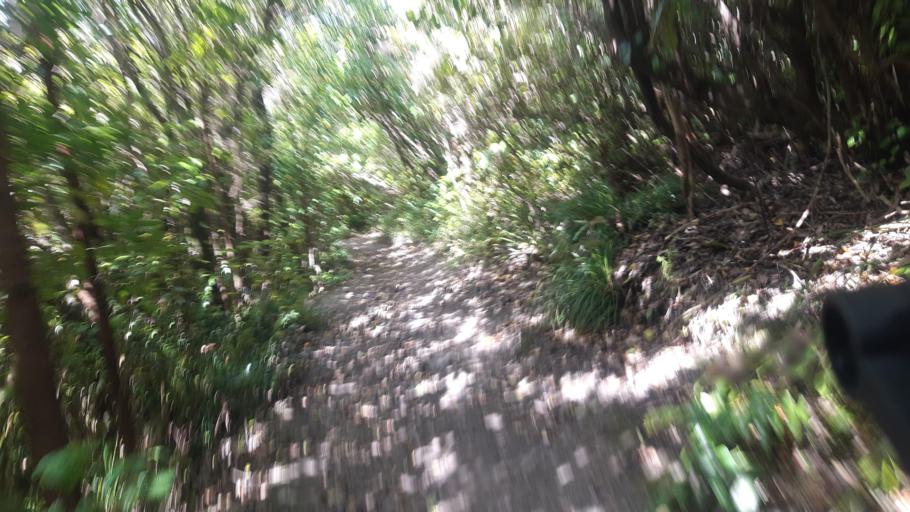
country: NZ
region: Marlborough
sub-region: Marlborough District
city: Picton
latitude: -41.2559
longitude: 174.0387
